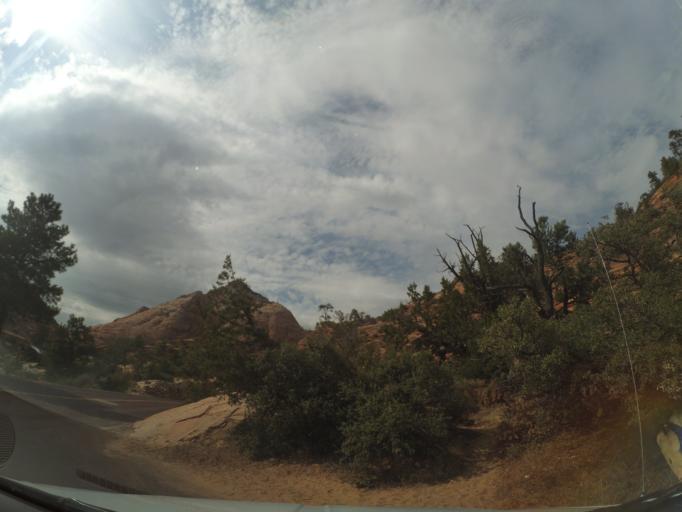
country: US
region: Utah
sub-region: Washington County
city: Hildale
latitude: 37.2140
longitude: -112.9337
